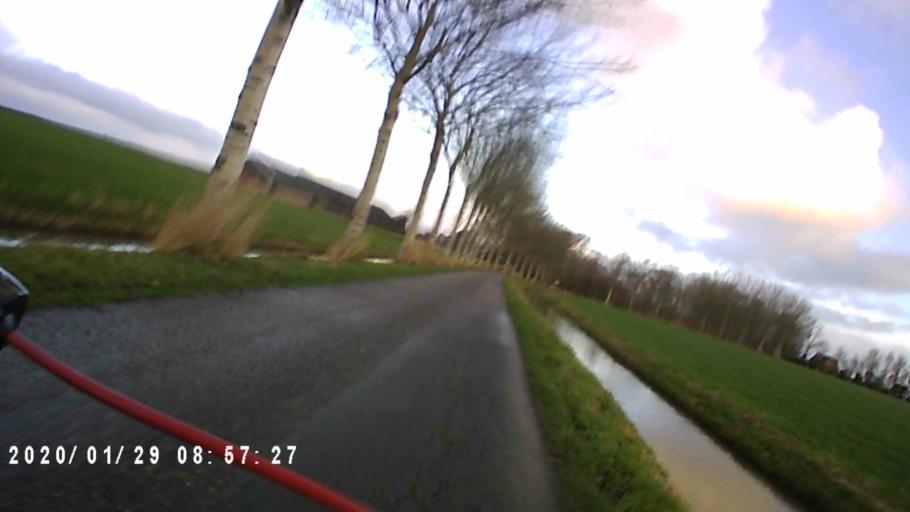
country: NL
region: Groningen
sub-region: Gemeente Zuidhorn
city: Aduard
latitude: 53.3162
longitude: 6.4547
